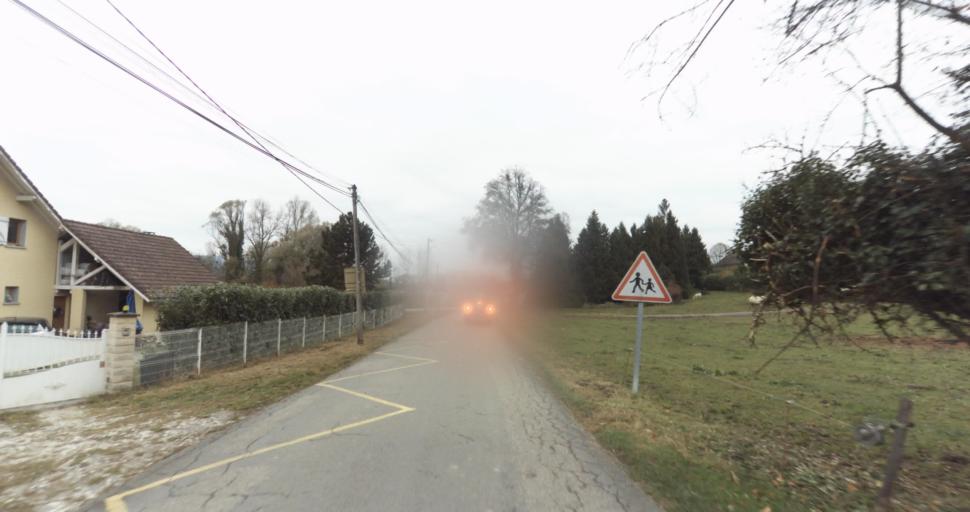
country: FR
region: Rhone-Alpes
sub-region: Departement de la Savoie
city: Albens
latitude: 45.7696
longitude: 5.9638
